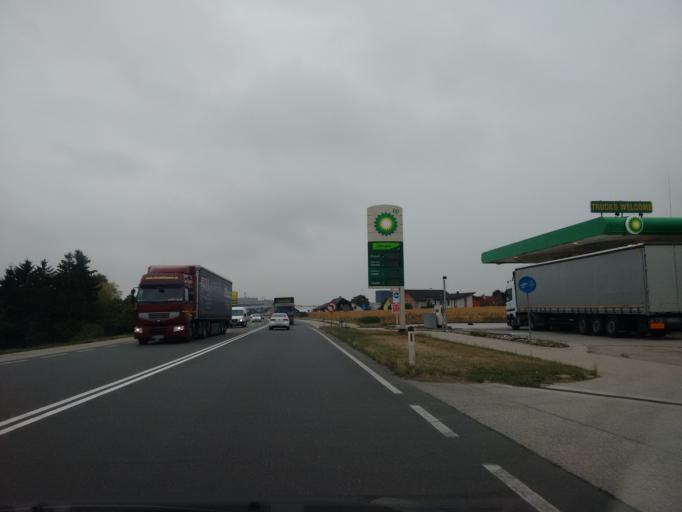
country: AT
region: Upper Austria
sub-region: Wels-Land
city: Marchtrenk
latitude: 48.1898
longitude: 14.1005
